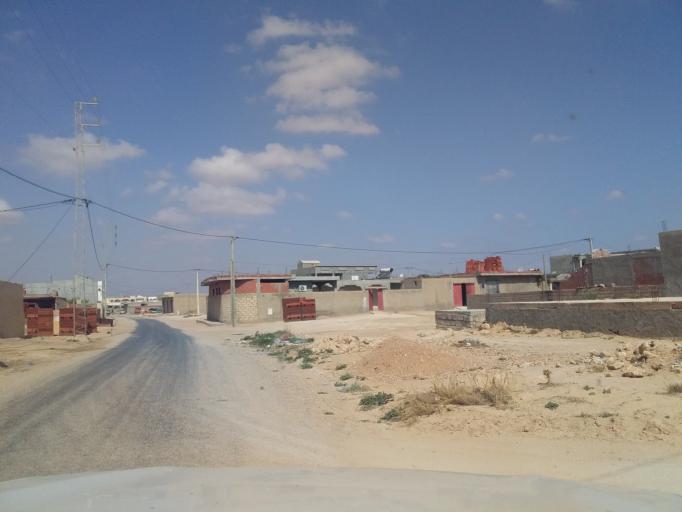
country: TN
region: Madanin
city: Medenine
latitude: 33.5821
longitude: 10.3280
